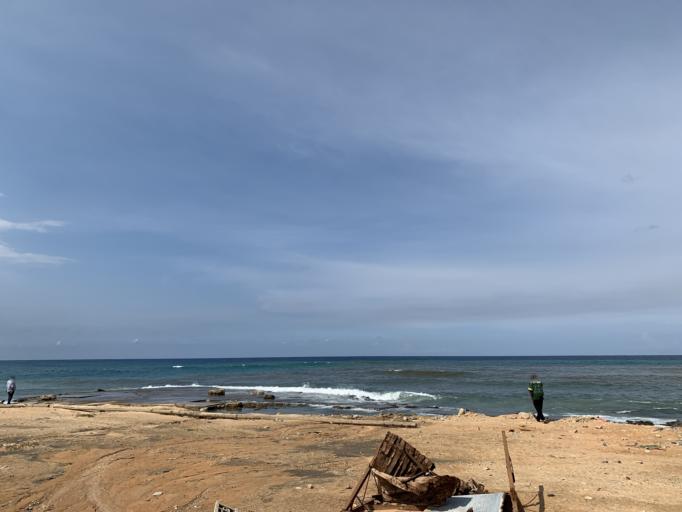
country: LY
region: Tripoli
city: Tripoli
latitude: 32.8635
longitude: 13.0903
